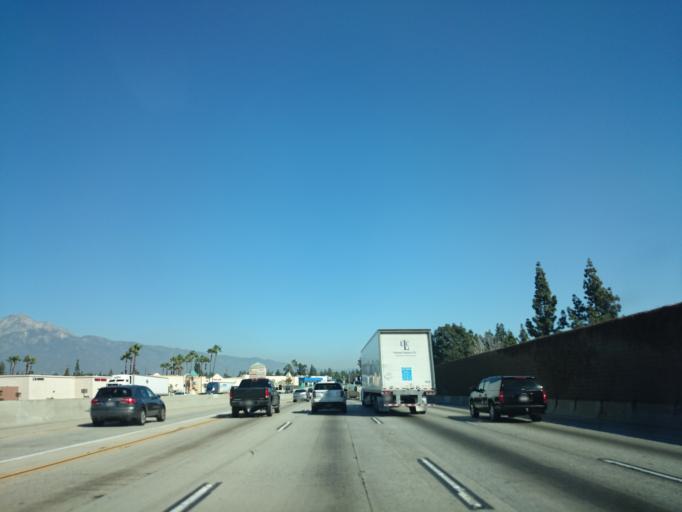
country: US
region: California
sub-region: San Bernardino County
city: Montclair
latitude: 34.0855
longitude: -117.6892
